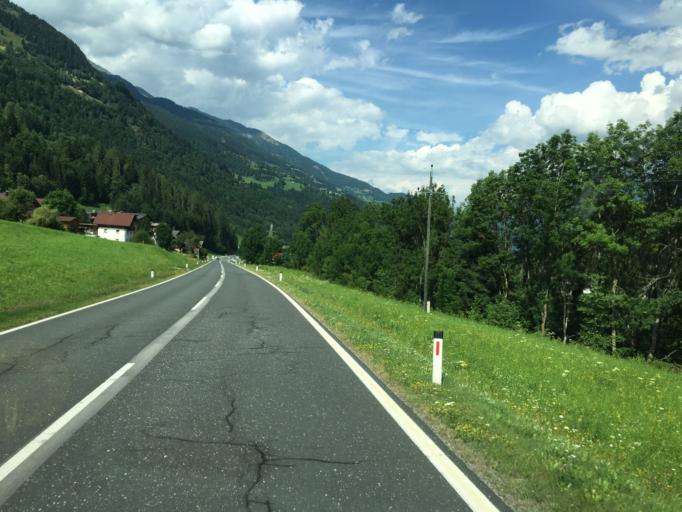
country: AT
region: Carinthia
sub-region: Politischer Bezirk Spittal an der Drau
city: Rangersdorf
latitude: 46.8625
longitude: 12.9668
